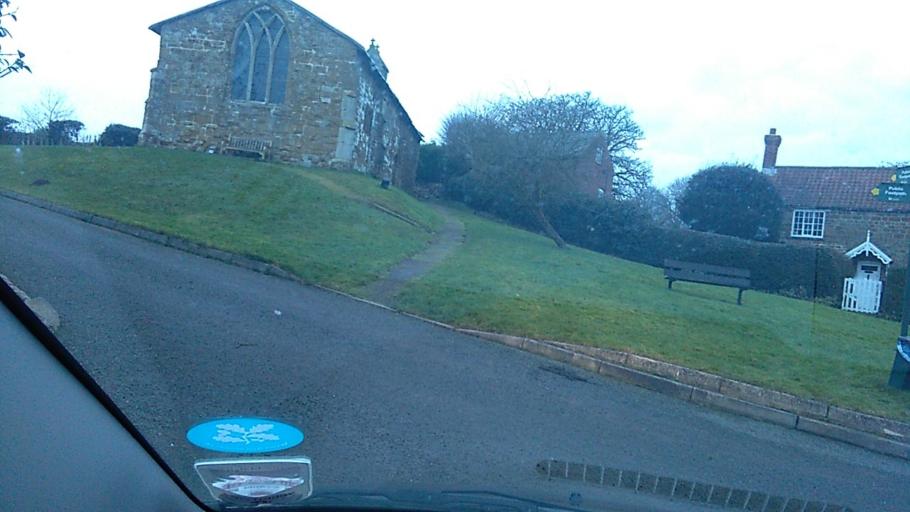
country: GB
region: England
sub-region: Leicestershire
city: Melton Mowbray
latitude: 52.8054
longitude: -0.9095
